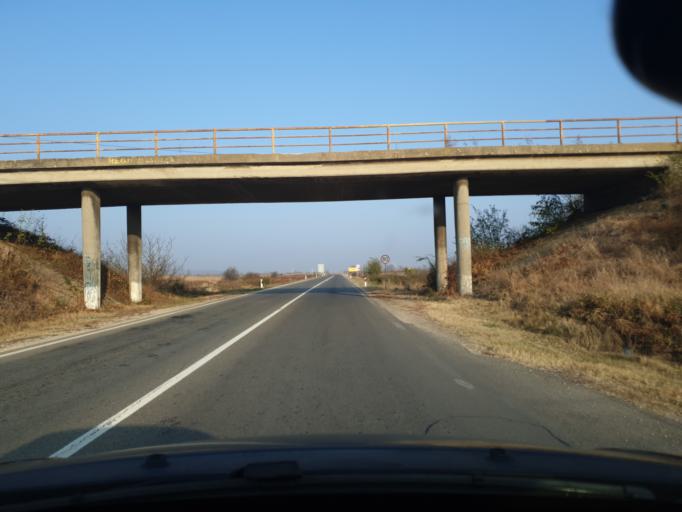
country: RS
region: Central Serbia
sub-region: Jablanicki Okrug
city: Leskovac
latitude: 42.9280
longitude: 22.0163
